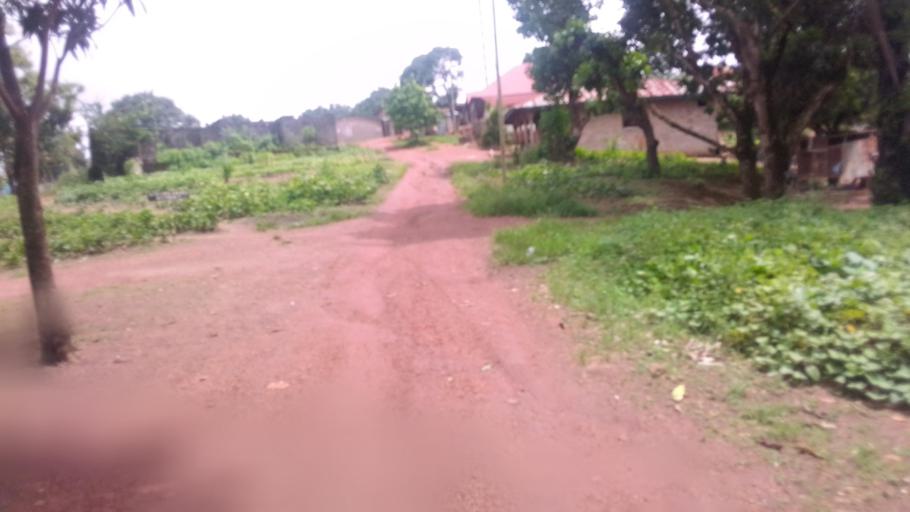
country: SL
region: Eastern Province
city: Kenema
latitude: 7.8575
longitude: -11.1871
